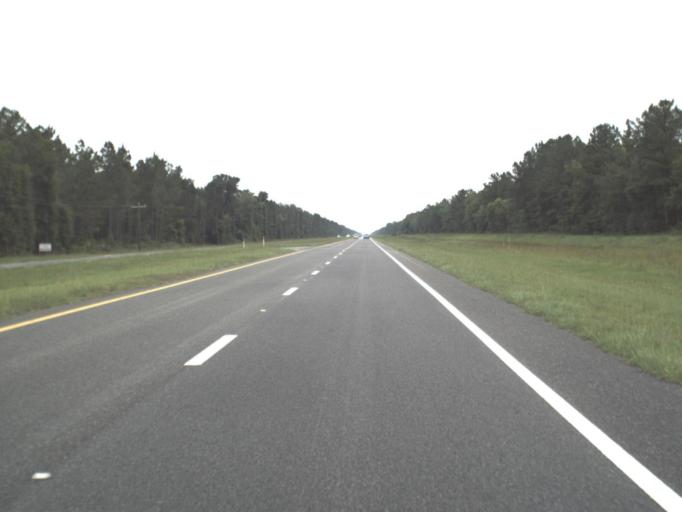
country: US
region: Florida
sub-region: Levy County
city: Chiefland
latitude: 29.3426
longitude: -82.7776
